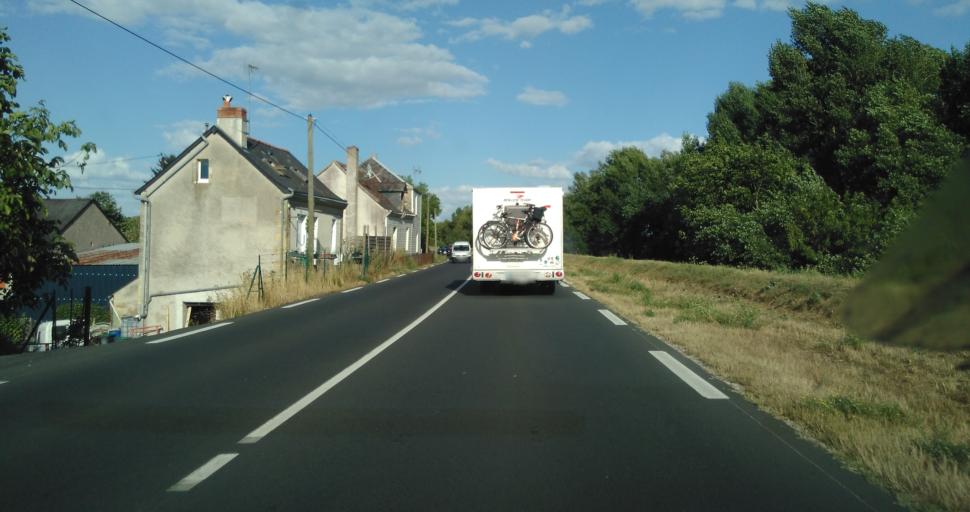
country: FR
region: Centre
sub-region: Departement d'Indre-et-Loire
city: Montlouis-sur-Loire
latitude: 47.3944
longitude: 0.8368
